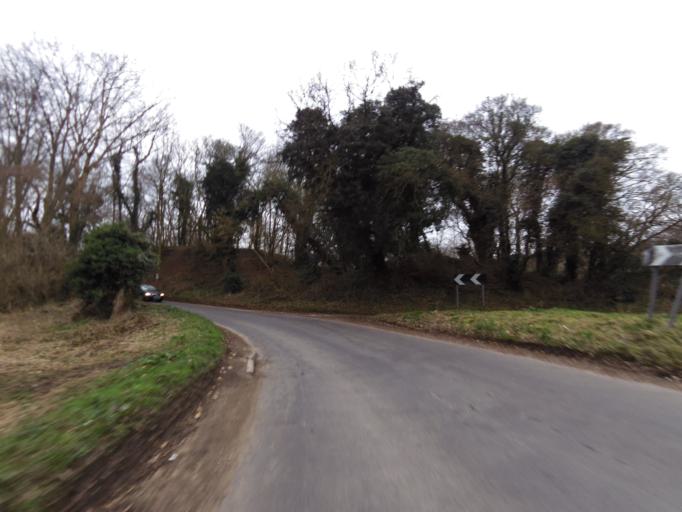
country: GB
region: England
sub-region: Suffolk
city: Wickham Market
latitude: 52.1595
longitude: 1.3549
